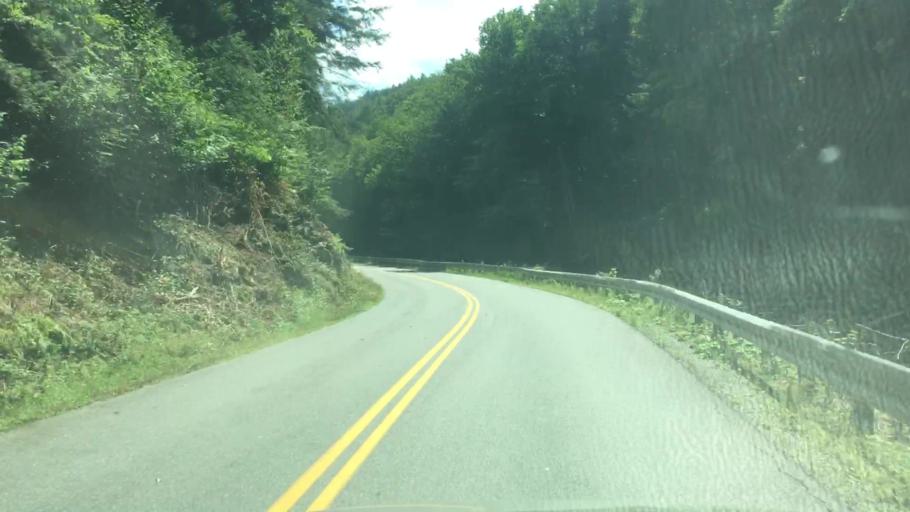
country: US
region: Vermont
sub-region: Windham County
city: West Brattleboro
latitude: 42.8140
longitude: -72.7355
